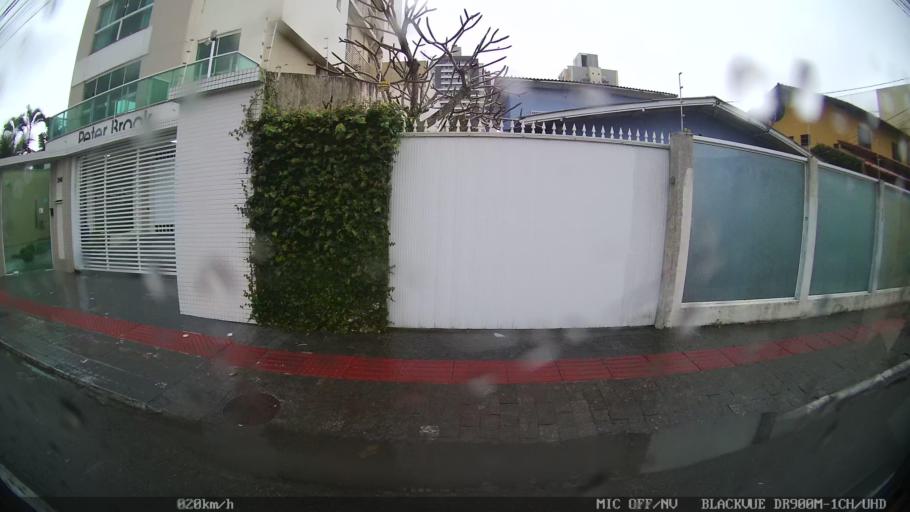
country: BR
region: Santa Catarina
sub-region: Itajai
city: Itajai
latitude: -26.9134
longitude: -48.6640
